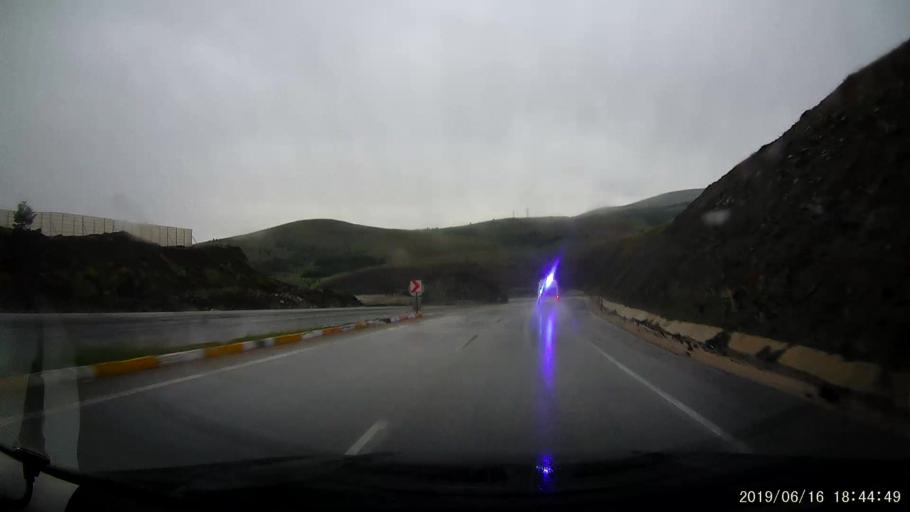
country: TR
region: Erzincan
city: Doganbeyli
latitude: 39.8701
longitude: 39.0666
